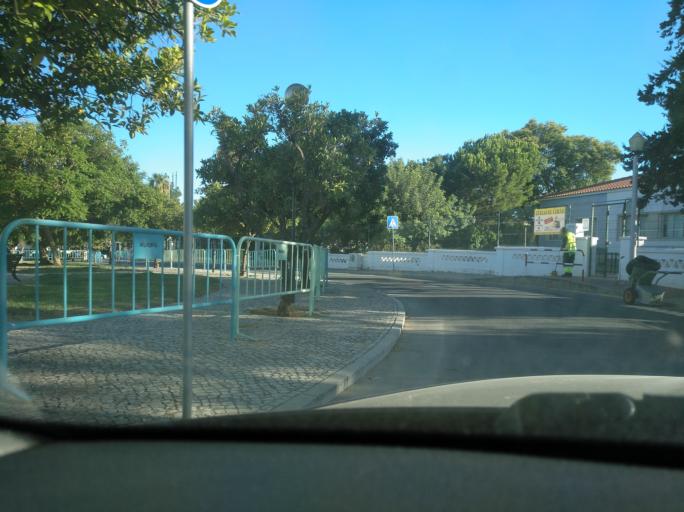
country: PT
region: Faro
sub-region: Vila Real de Santo Antonio
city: Monte Gordo
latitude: 37.1756
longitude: -7.5357
